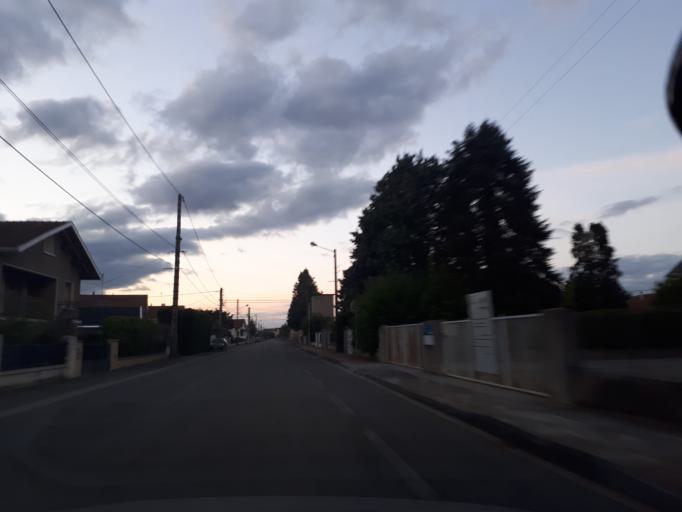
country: FR
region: Rhone-Alpes
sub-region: Departement de la Loire
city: Feurs
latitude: 45.7373
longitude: 4.2341
